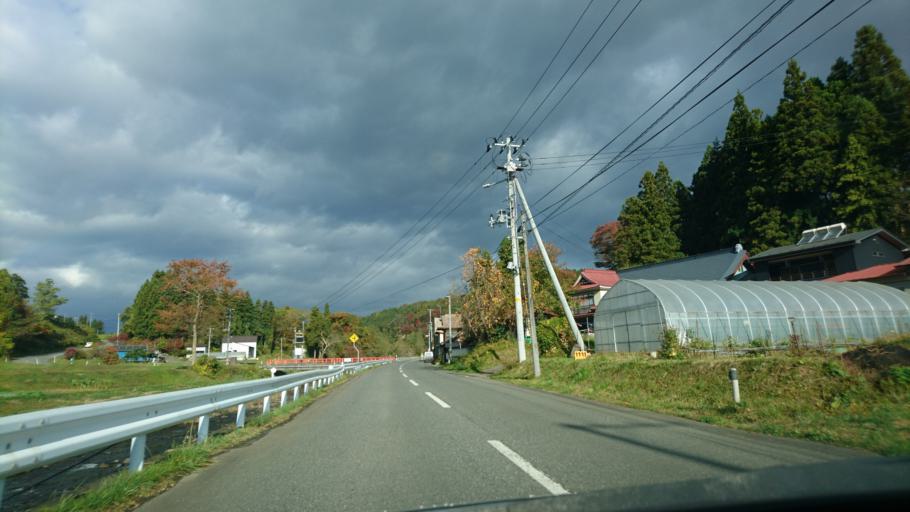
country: JP
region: Iwate
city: Mizusawa
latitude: 39.0792
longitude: 141.0010
